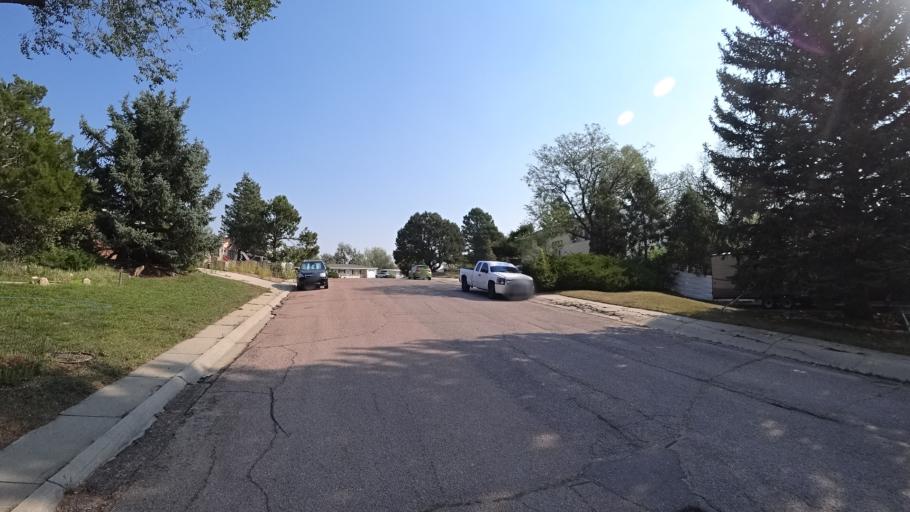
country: US
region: Colorado
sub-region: El Paso County
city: Colorado Springs
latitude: 38.8077
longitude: -104.8387
